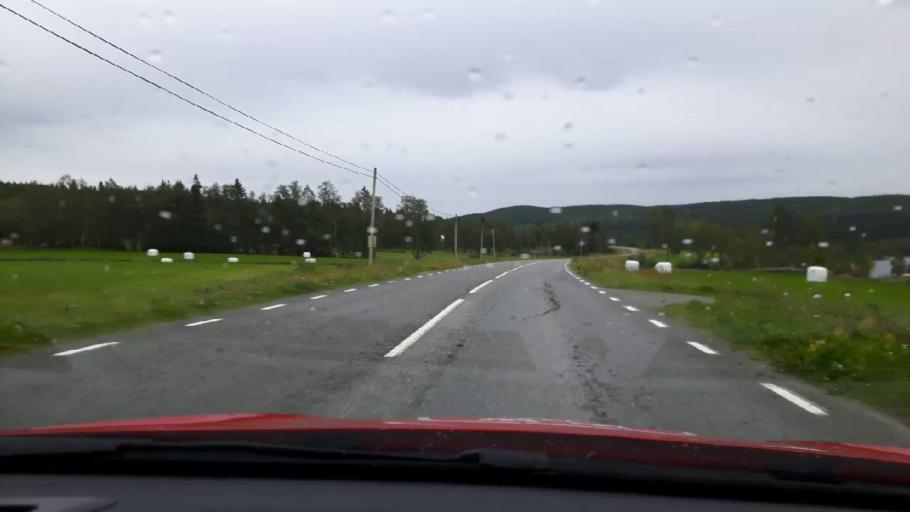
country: SE
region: Jaemtland
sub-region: Are Kommun
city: Jarpen
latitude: 63.4052
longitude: 13.3702
